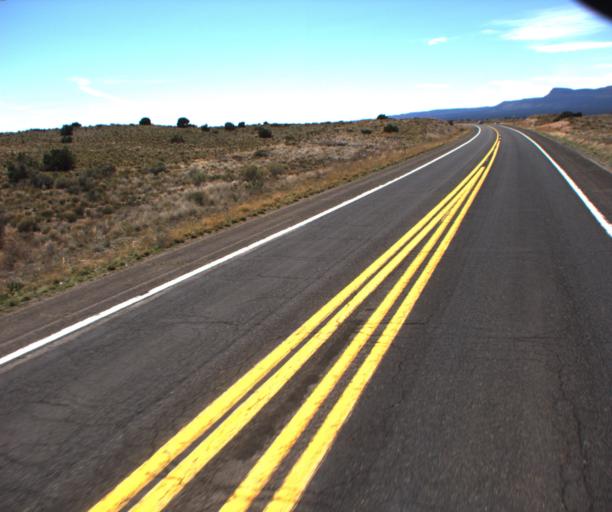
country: US
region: Arizona
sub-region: Mohave County
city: Peach Springs
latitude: 35.5241
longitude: -113.4766
